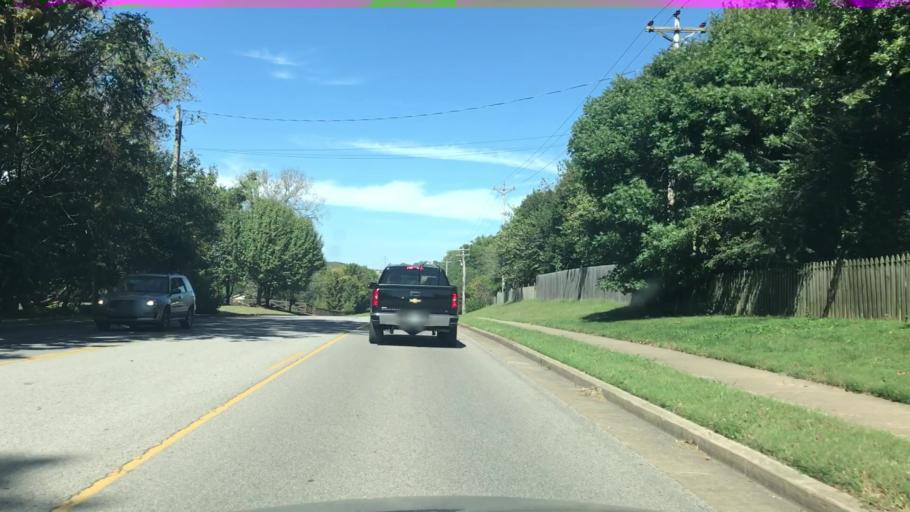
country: US
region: Tennessee
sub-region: Williamson County
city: Franklin
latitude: 35.9027
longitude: -86.8250
